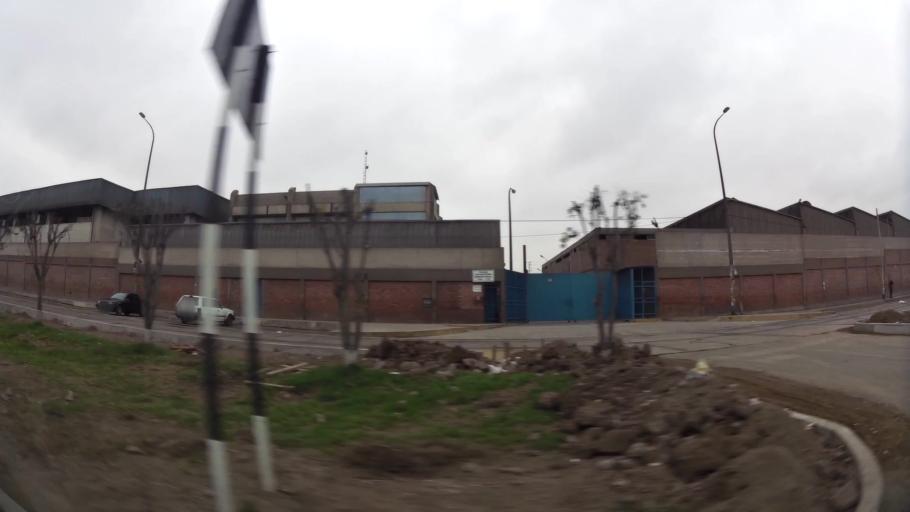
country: PE
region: Lima
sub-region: Lima
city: Vitarte
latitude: -12.0501
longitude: -76.9568
